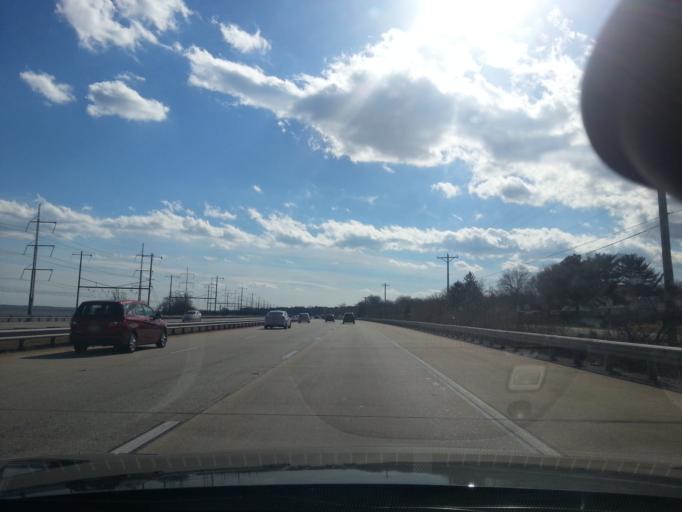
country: US
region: Delaware
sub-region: New Castle County
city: Claymont
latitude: 39.7877
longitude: -75.4689
